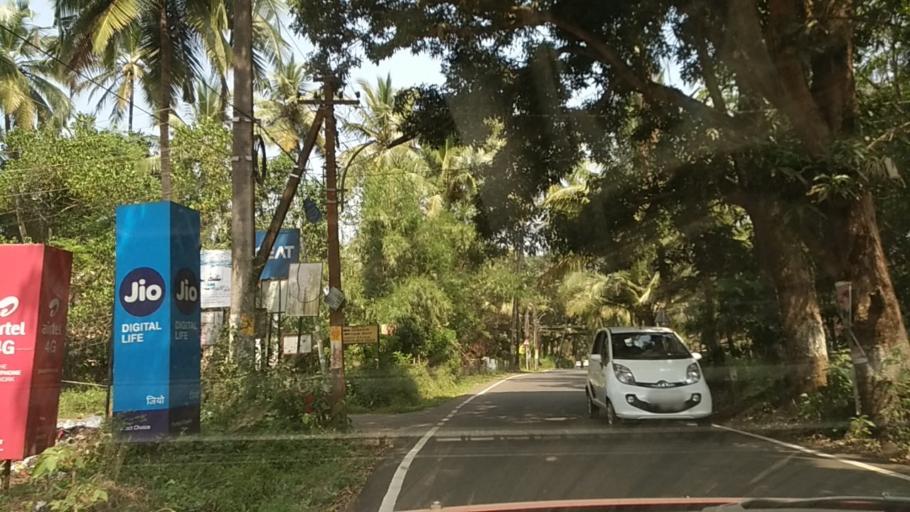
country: IN
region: Goa
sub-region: South Goa
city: Colva
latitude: 15.2872
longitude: 73.9204
